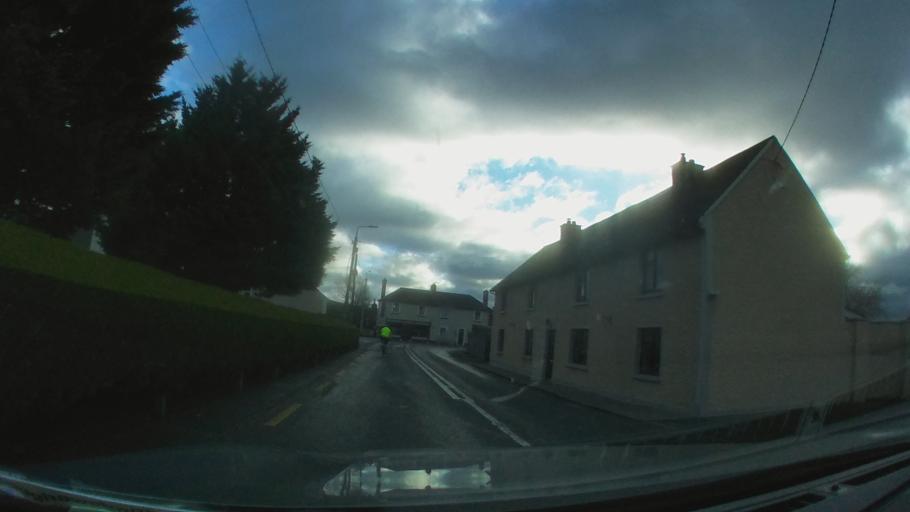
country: IE
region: Leinster
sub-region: Kilkenny
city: Thomastown
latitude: 52.5875
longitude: -7.0956
